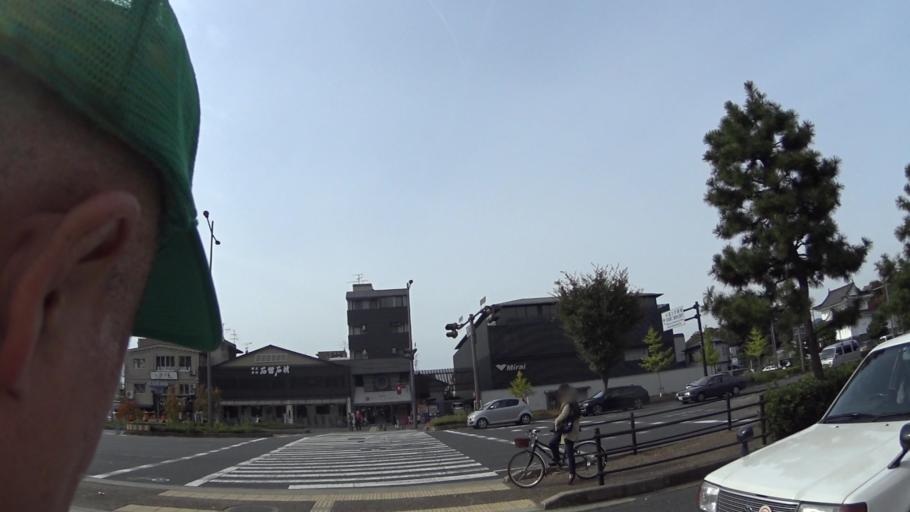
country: JP
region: Kyoto
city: Kyoto
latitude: 35.0113
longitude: 135.7520
